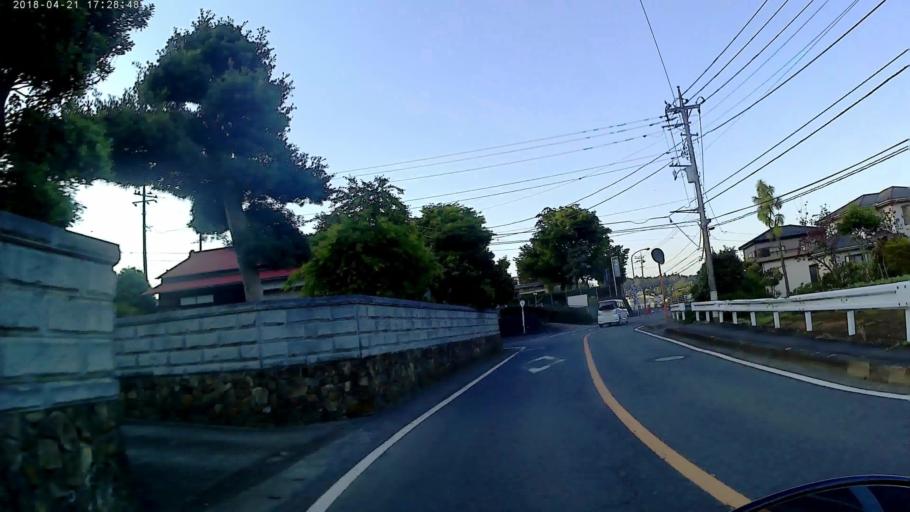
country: JP
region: Kanagawa
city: Atsugi
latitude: 35.4252
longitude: 139.4125
